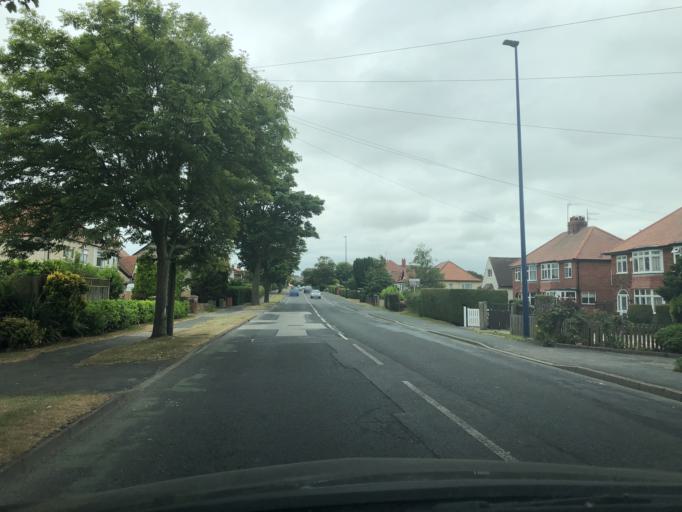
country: GB
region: England
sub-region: North Yorkshire
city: Filey
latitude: 54.2086
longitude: -0.2974
